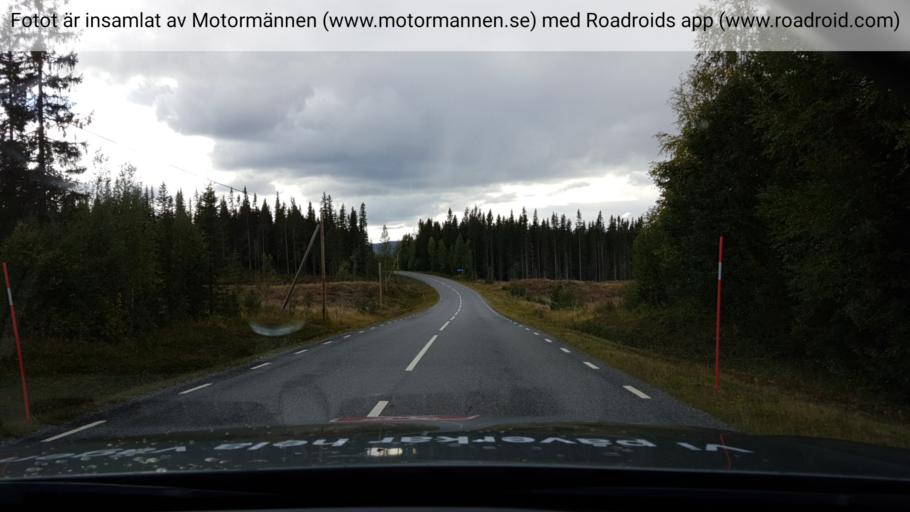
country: SE
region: Jaemtland
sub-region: Are Kommun
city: Are
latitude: 63.5873
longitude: 13.0258
